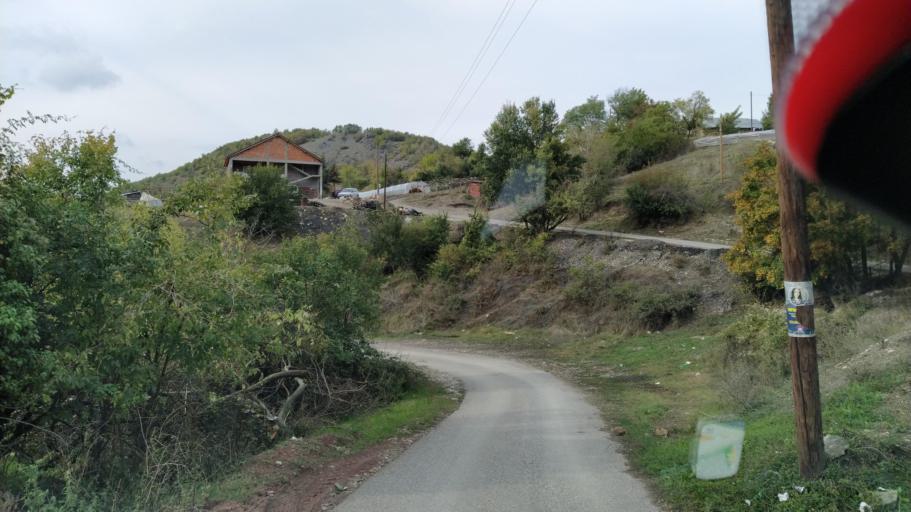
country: MK
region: Strumica
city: Veljusa
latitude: 41.5127
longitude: 22.4915
